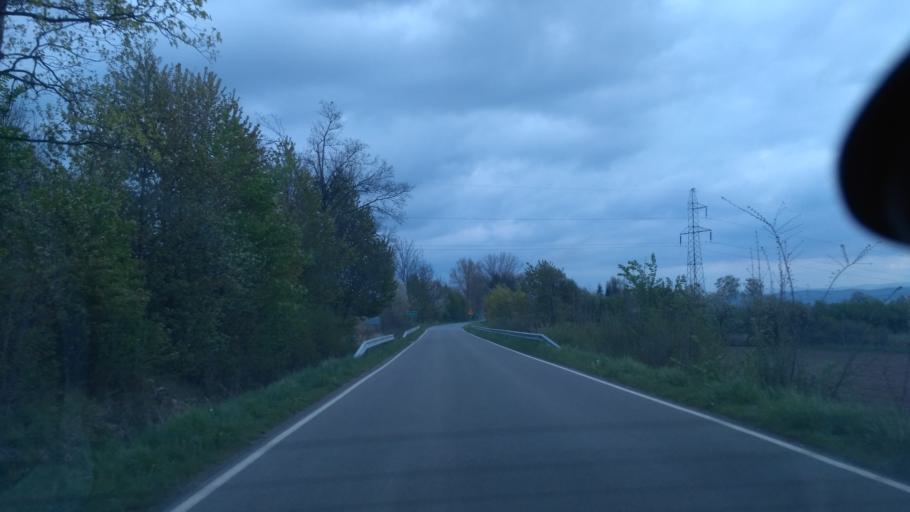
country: PL
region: Subcarpathian Voivodeship
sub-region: Powiat brzozowski
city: Turze Pole
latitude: 49.6352
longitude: 22.0047
